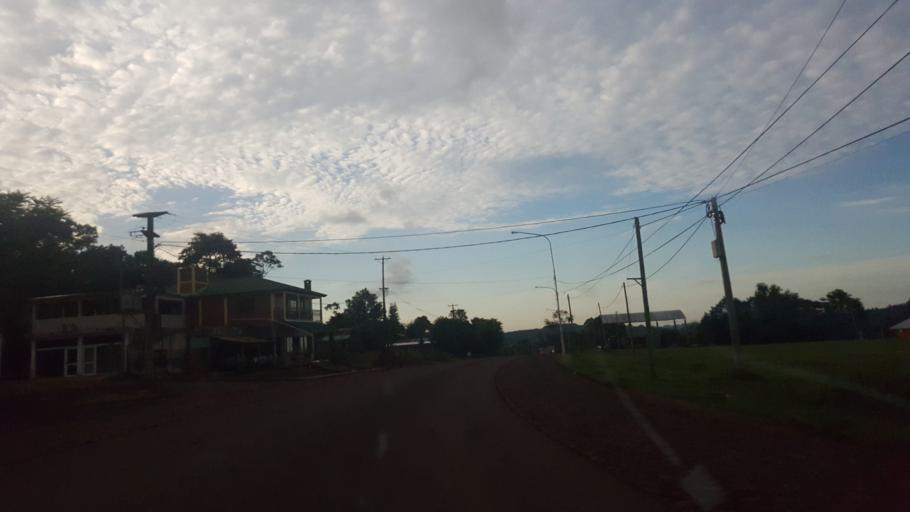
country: AR
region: Misiones
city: Dos de Mayo
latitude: -27.0309
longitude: -54.6862
